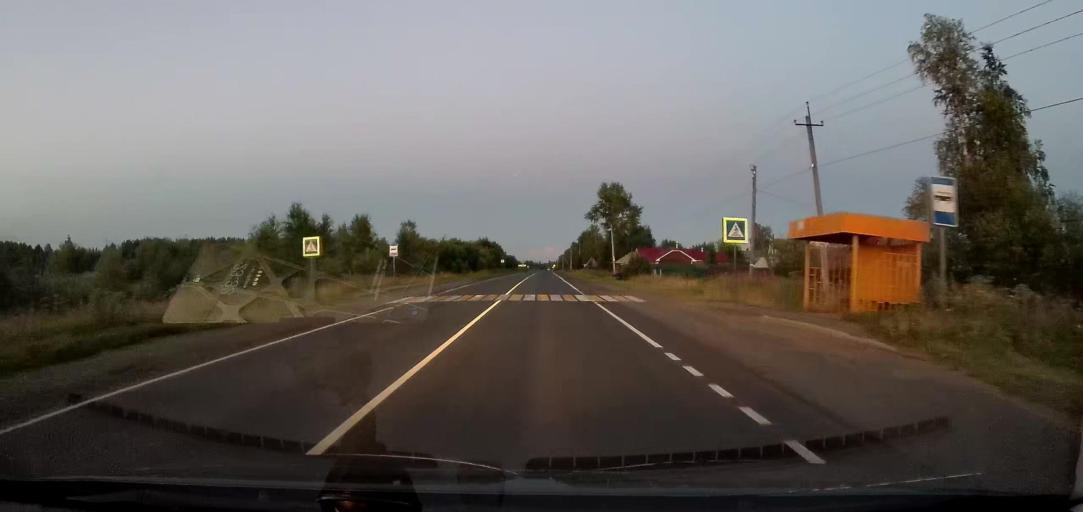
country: RU
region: Arkhangelskaya
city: Uyemskiy
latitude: 64.4464
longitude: 40.9480
